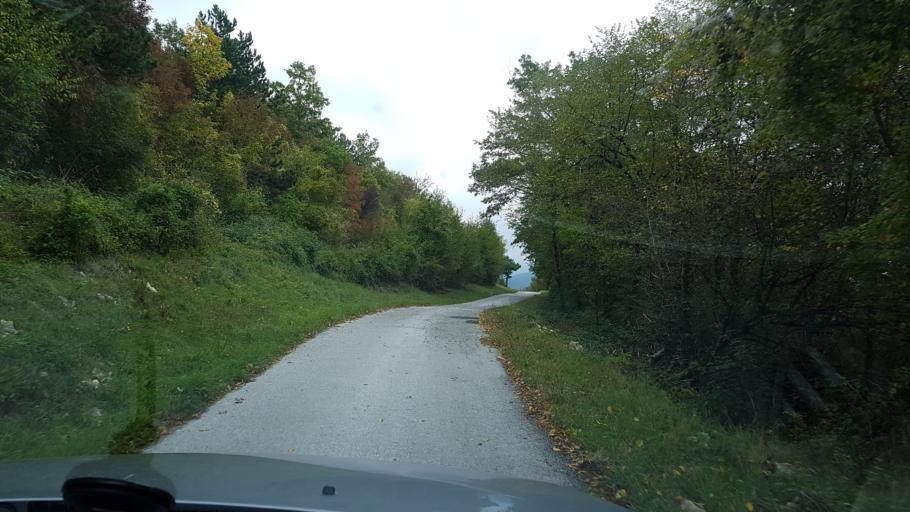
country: HR
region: Istarska
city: Buzet
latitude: 45.4491
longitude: 14.0245
